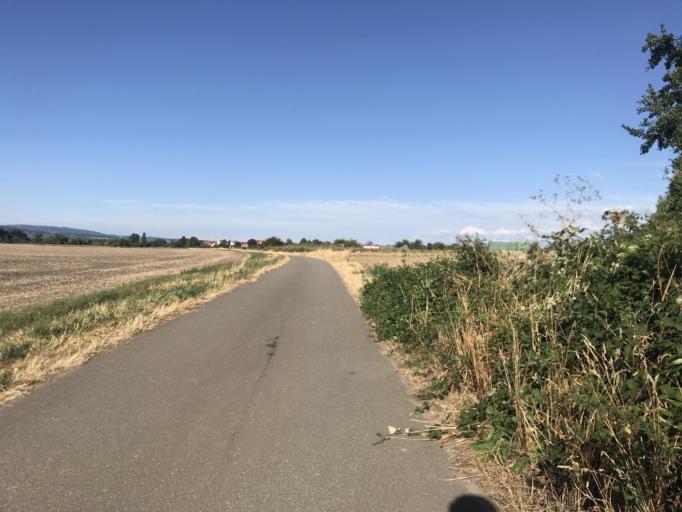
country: DE
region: Rheinland-Pfalz
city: Gau-Algesheim
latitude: 49.9715
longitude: 7.9986
